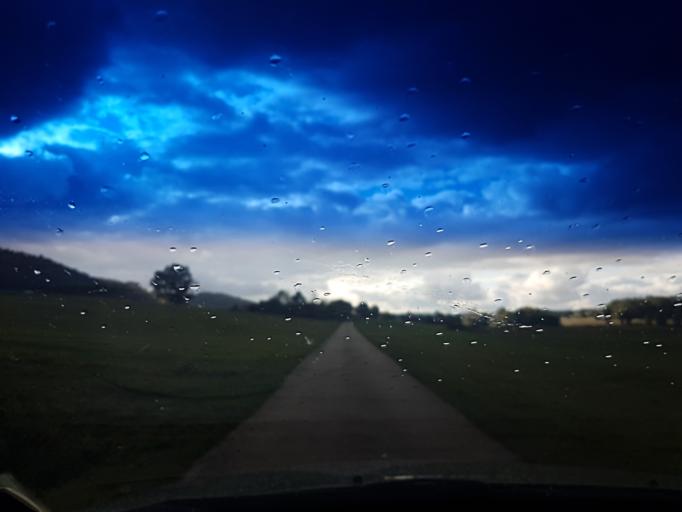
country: DE
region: Bavaria
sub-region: Regierungsbezirk Mittelfranken
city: Burghaslach
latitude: 49.7648
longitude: 10.5453
